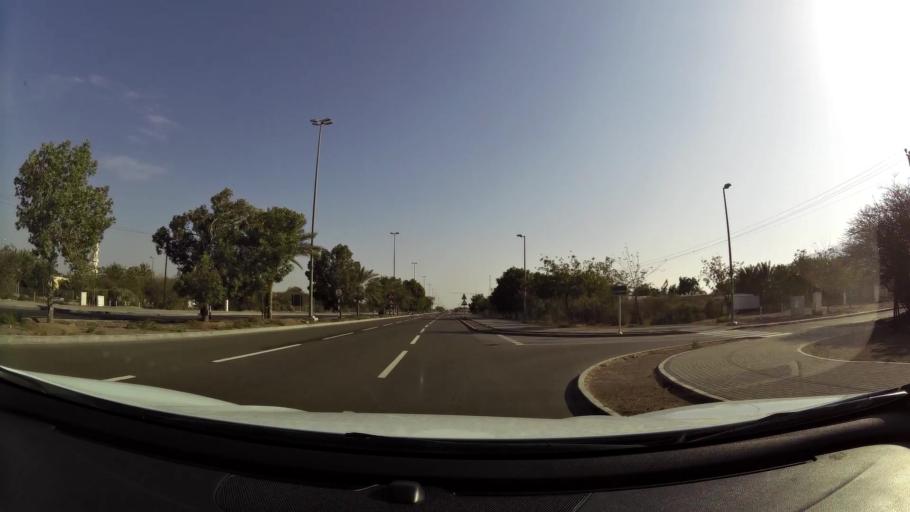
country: AE
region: Abu Dhabi
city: Al Ain
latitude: 24.0441
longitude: 55.8425
